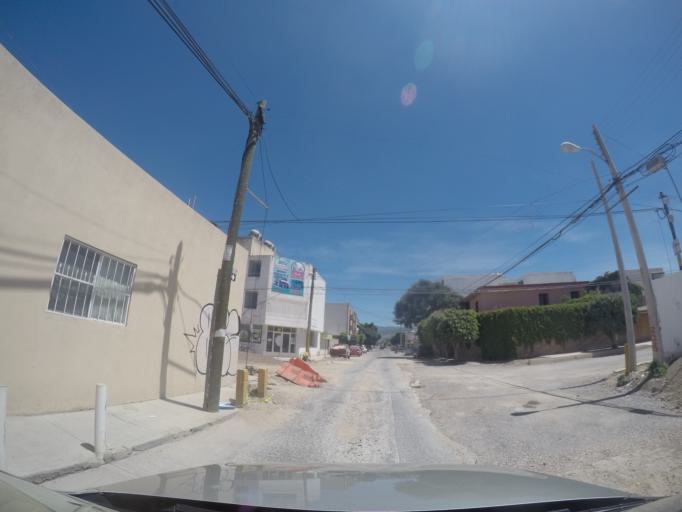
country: MX
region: San Luis Potosi
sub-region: San Luis Potosi
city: San Luis Potosi
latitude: 22.1560
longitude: -100.9939
